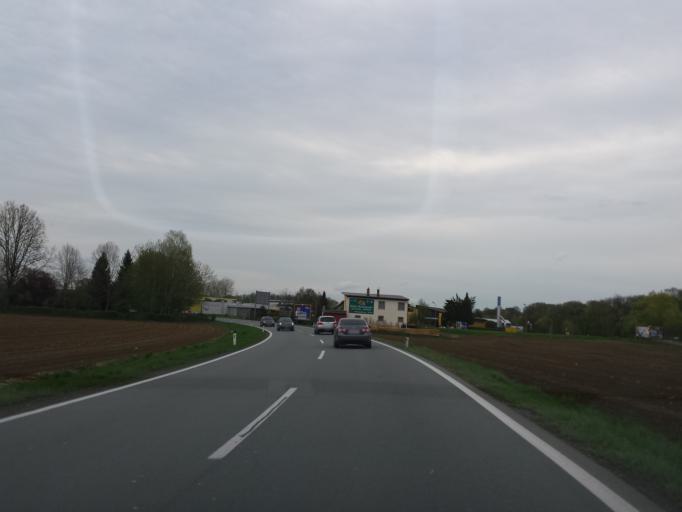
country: AT
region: Styria
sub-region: Politischer Bezirk Hartberg-Fuerstenfeld
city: Fuerstenfeld
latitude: 47.0495
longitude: 16.0868
